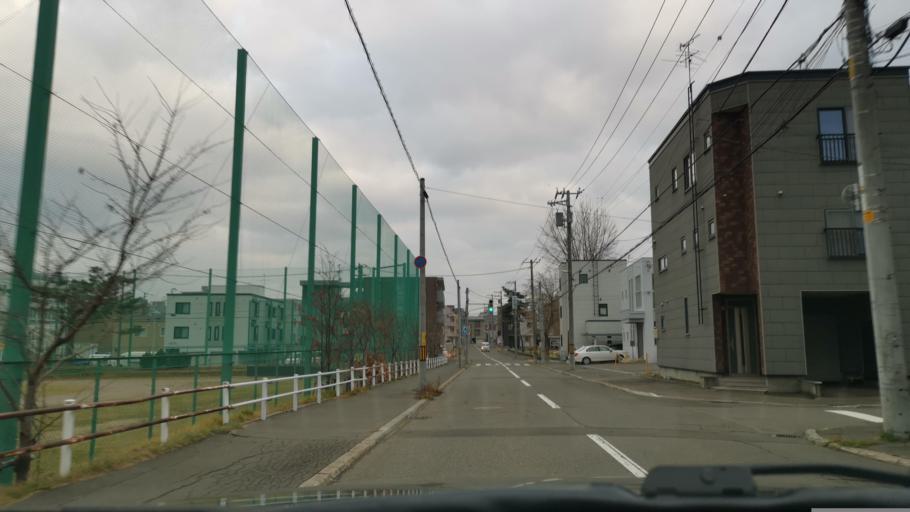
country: JP
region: Hokkaido
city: Sapporo
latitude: 43.0446
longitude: 141.4060
